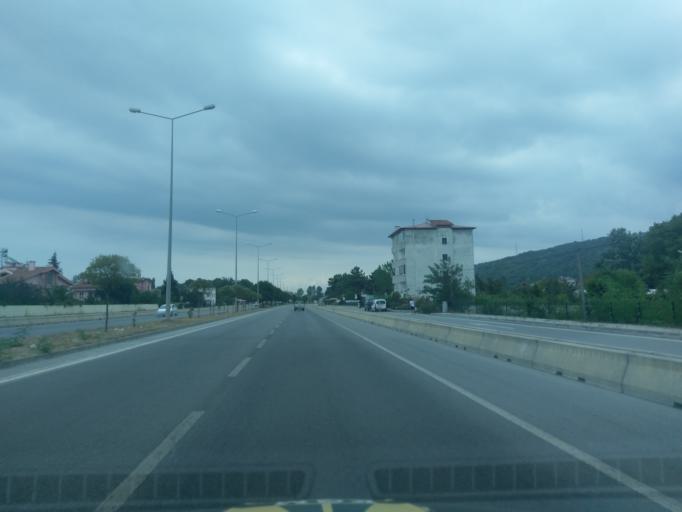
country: TR
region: Samsun
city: Taflan
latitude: 41.3978
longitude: 36.1952
